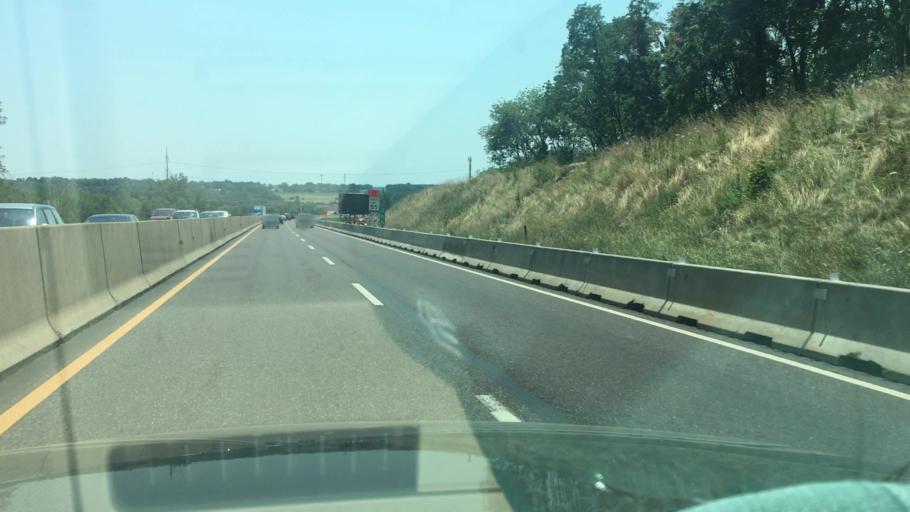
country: US
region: Pennsylvania
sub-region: Montgomery County
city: Telford
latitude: 40.3390
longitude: -75.3845
